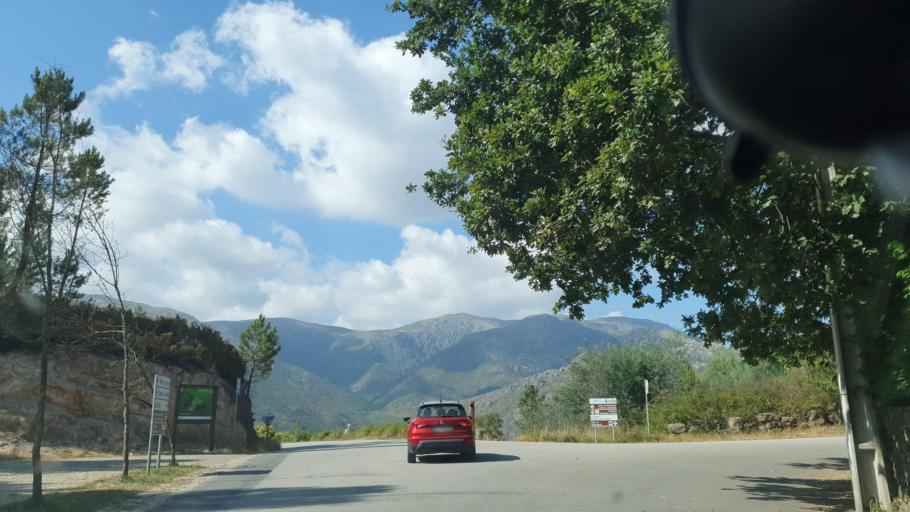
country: PT
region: Braga
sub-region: Terras de Bouro
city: Antas
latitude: 41.7668
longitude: -8.1902
